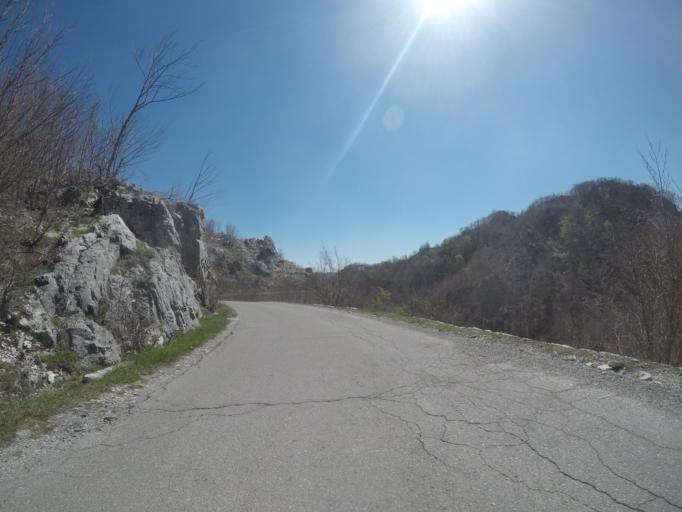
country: ME
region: Cetinje
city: Cetinje
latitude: 42.4355
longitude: 18.8611
